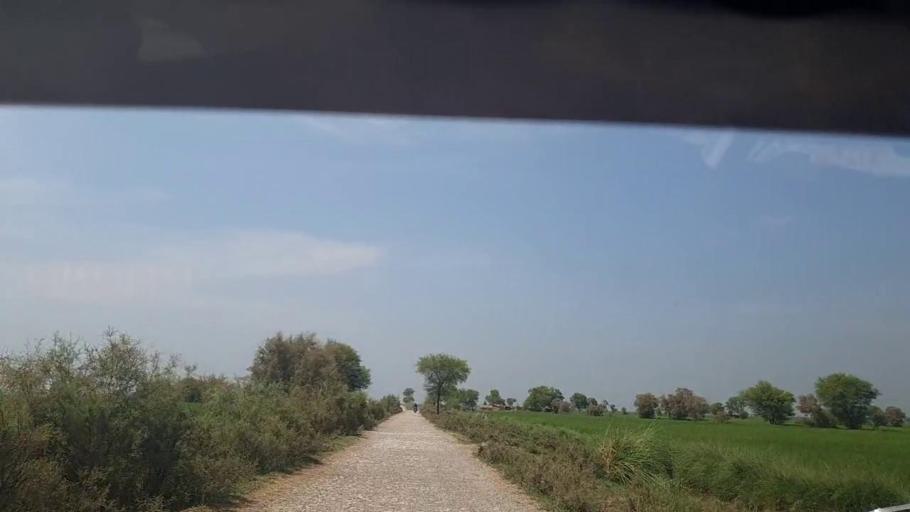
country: PK
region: Sindh
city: Thul
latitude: 28.2083
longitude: 68.6905
